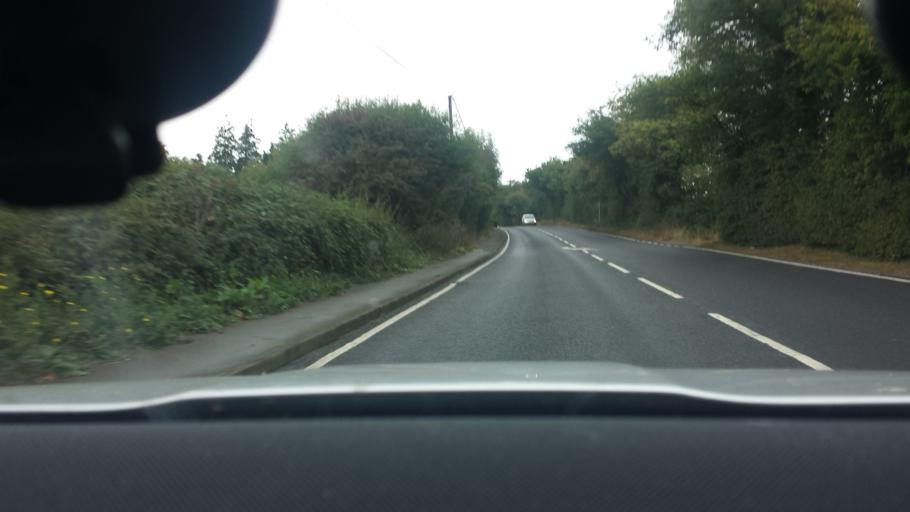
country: GB
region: England
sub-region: Kent
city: Staplehurst
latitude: 51.1731
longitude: 0.5526
